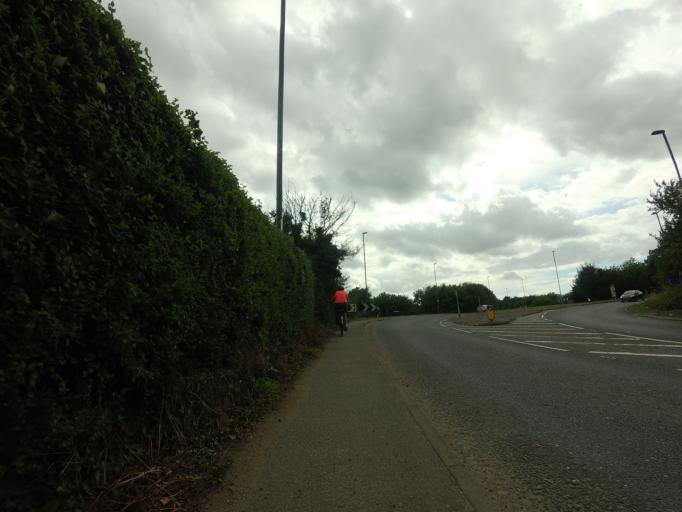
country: GB
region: England
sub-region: Medway
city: High Halstow
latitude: 51.4440
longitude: 0.5805
